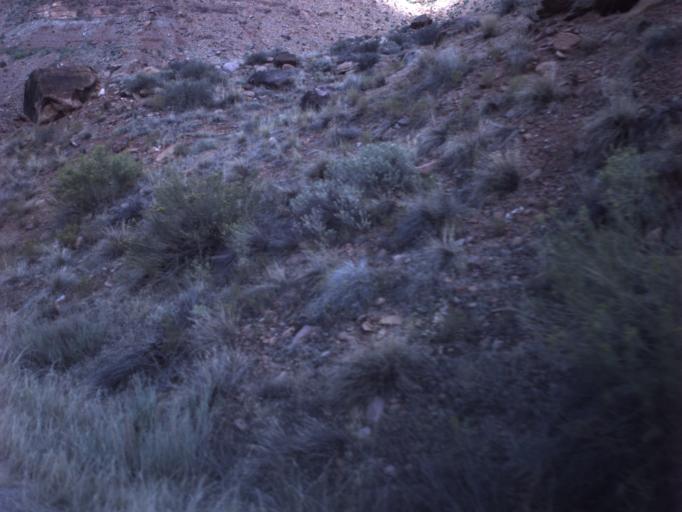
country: US
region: Utah
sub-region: Grand County
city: Moab
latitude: 38.6351
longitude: -109.4825
